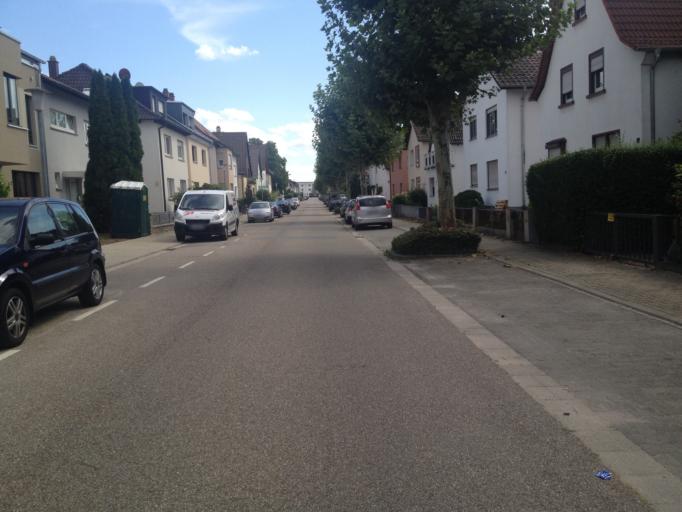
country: DE
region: Baden-Wuerttemberg
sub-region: Karlsruhe Region
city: Schwetzingen
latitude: 49.3769
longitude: 8.5766
